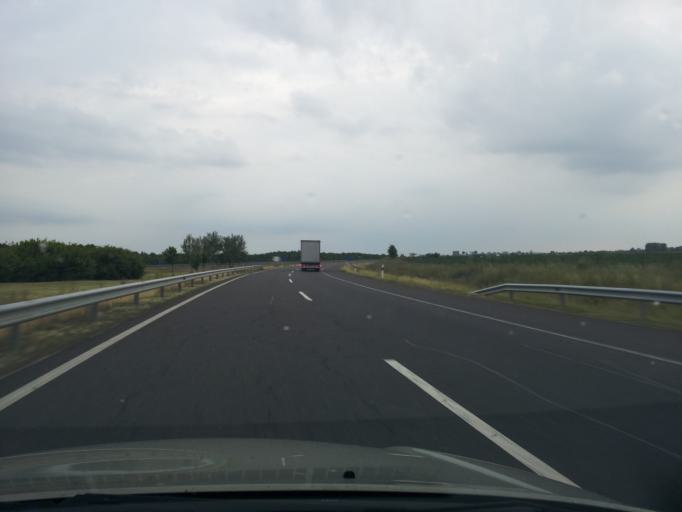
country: HU
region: Borsod-Abauj-Zemplen
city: Emod
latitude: 47.8816
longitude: 20.8310
